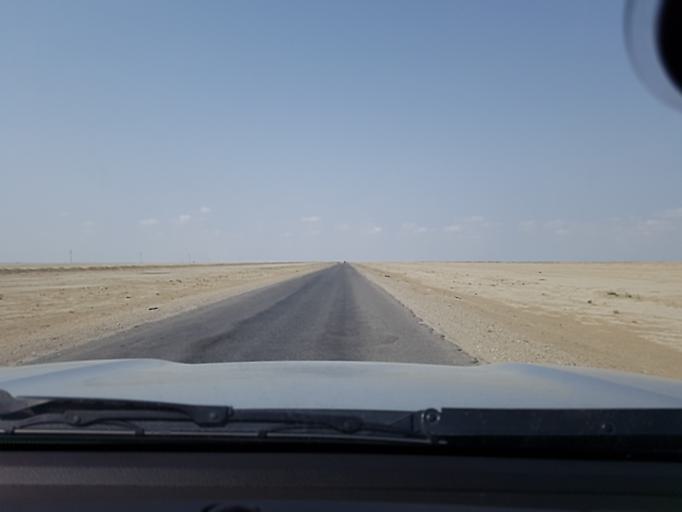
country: TM
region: Balkan
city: Gumdag
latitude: 38.6738
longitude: 54.4087
